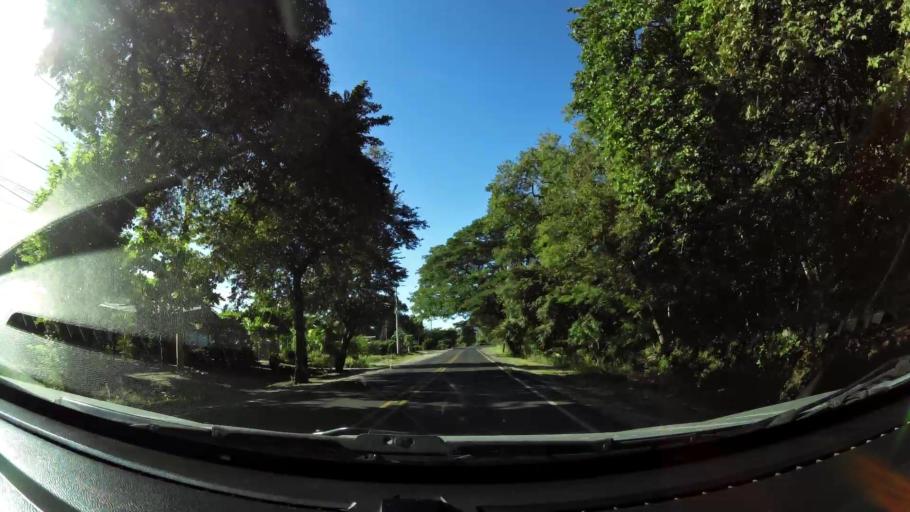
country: CR
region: Guanacaste
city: Belen
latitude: 10.4144
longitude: -85.5774
